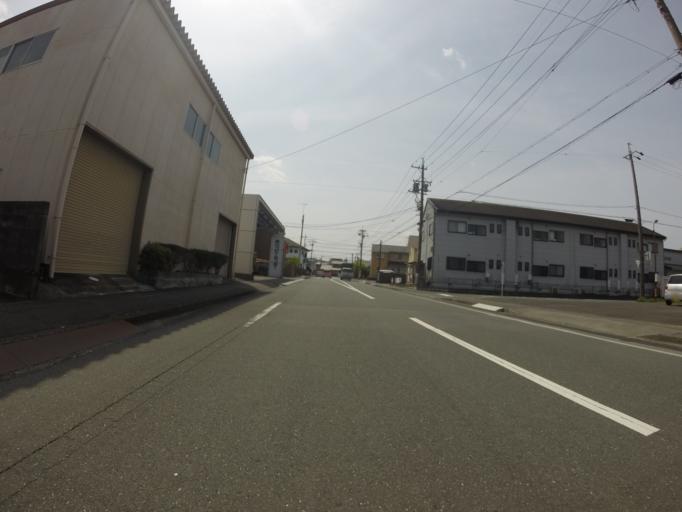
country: JP
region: Shizuoka
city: Kakegawa
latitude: 34.7722
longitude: 138.0032
